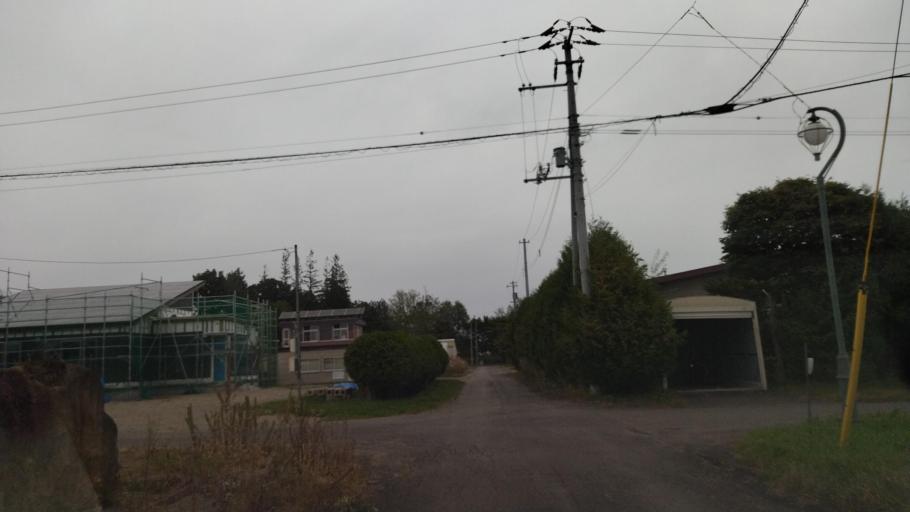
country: JP
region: Hokkaido
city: Otofuke
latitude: 43.2271
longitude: 143.2806
